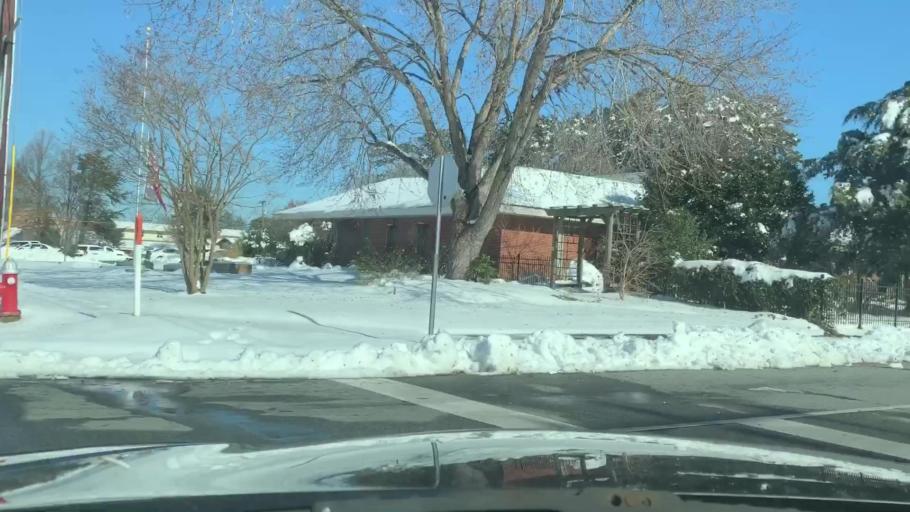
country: US
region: North Carolina
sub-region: Alamance County
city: Graham
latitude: 36.0972
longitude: -79.4059
